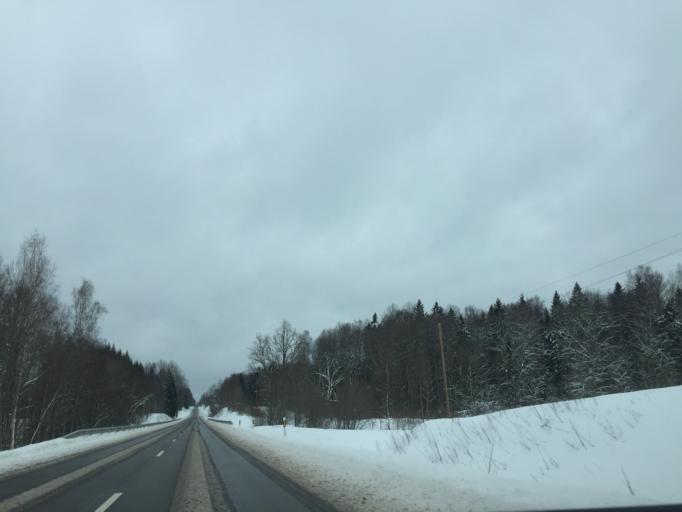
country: LV
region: Ligatne
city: Ligatne
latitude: 57.1356
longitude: 25.0839
